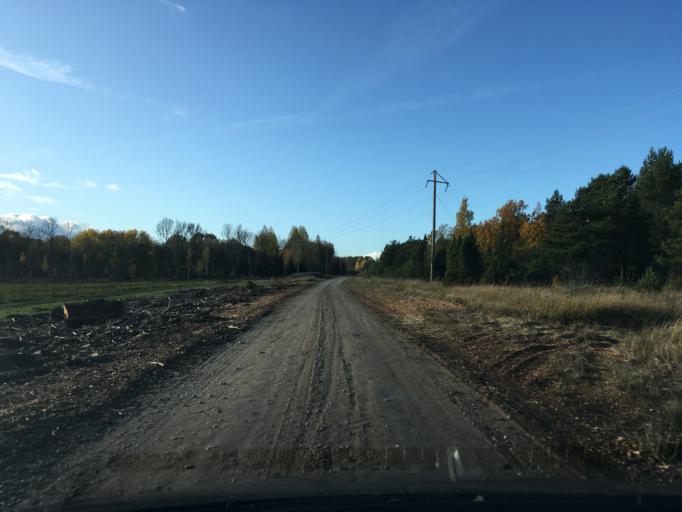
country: EE
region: Laeaene
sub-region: Lihula vald
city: Lihula
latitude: 58.5648
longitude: 23.7707
